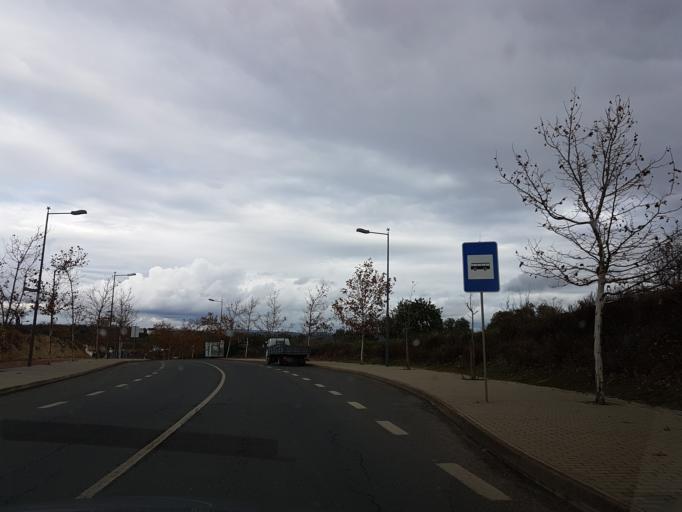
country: PT
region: Faro
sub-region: Albufeira
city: Ferreiras
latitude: 37.1206
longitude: -8.2242
